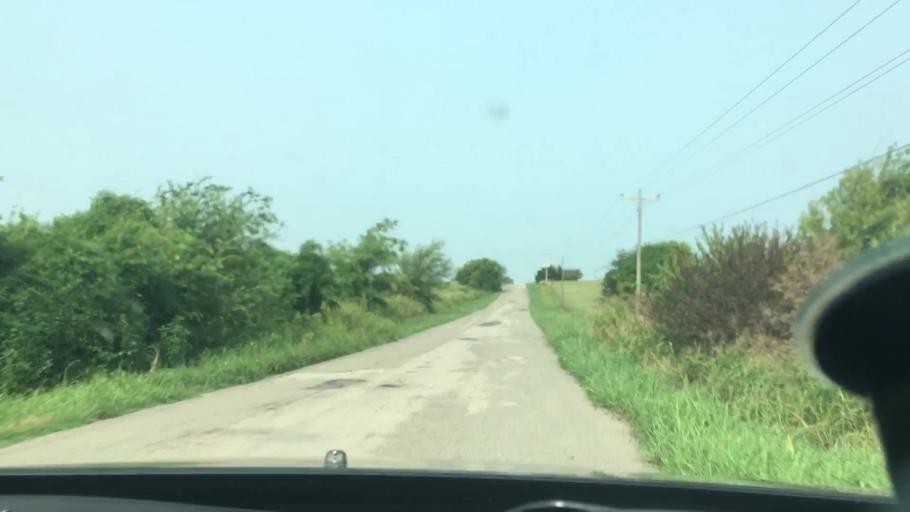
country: US
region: Oklahoma
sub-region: Garvin County
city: Lindsay
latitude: 34.8120
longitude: -97.6358
